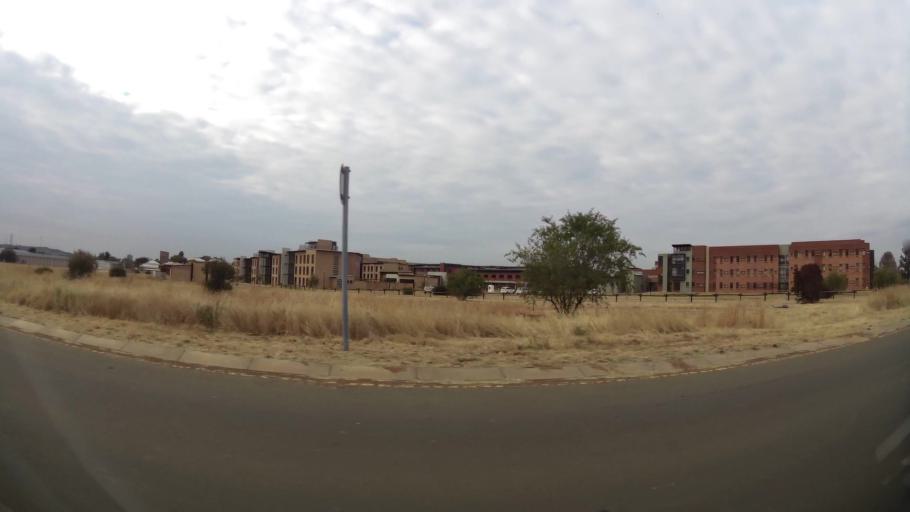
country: ZA
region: Orange Free State
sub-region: Mangaung Metropolitan Municipality
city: Bloemfontein
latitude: -29.1073
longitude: 26.1802
